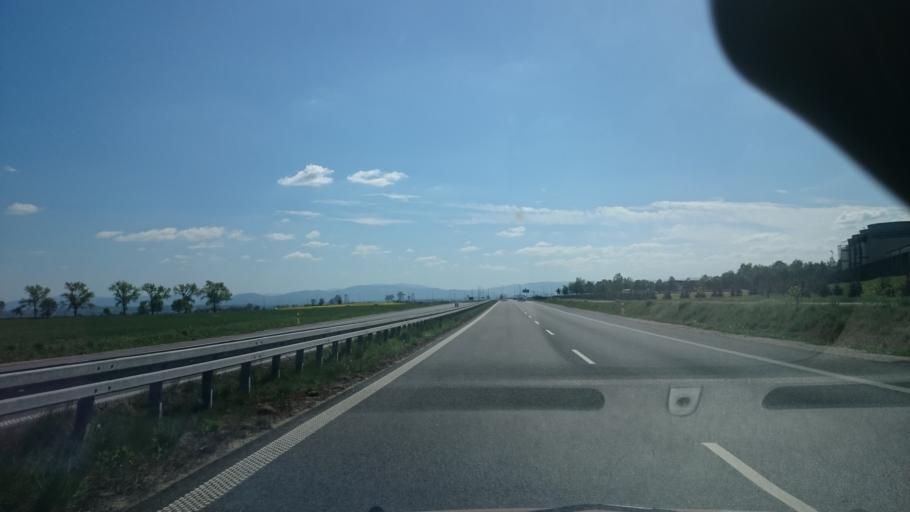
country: PL
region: Opole Voivodeship
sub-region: Powiat nyski
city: Nysa
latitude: 50.4805
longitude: 17.2653
